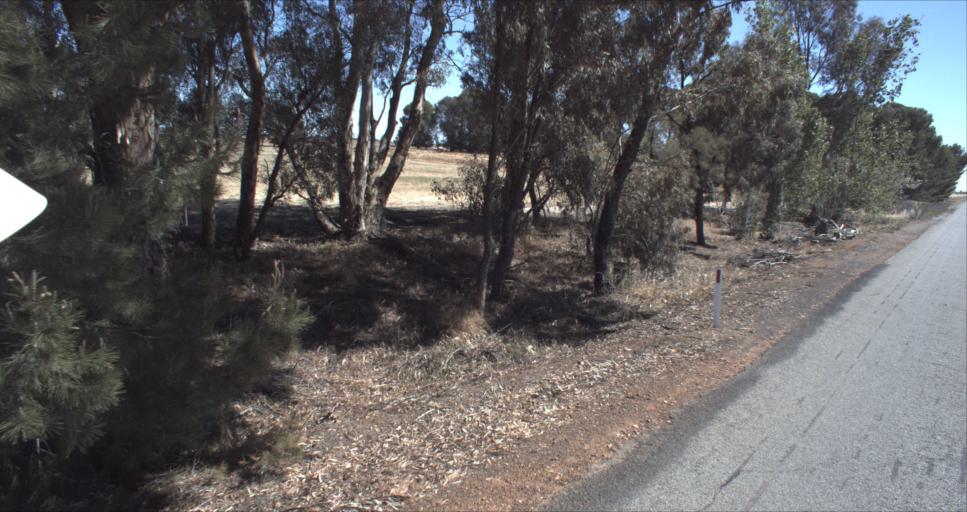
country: AU
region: New South Wales
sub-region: Leeton
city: Leeton
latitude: -34.5735
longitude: 146.3102
